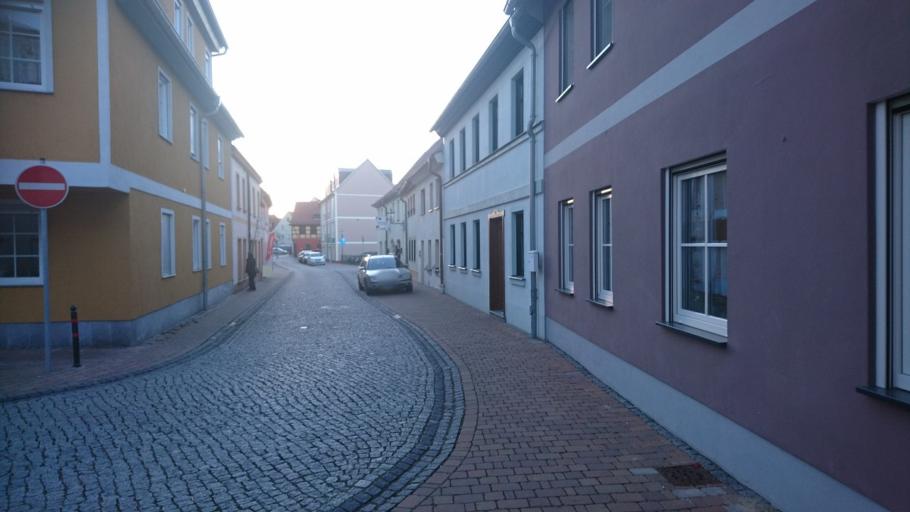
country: DE
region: Saxony
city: Bad Duben
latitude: 51.5919
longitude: 12.5869
